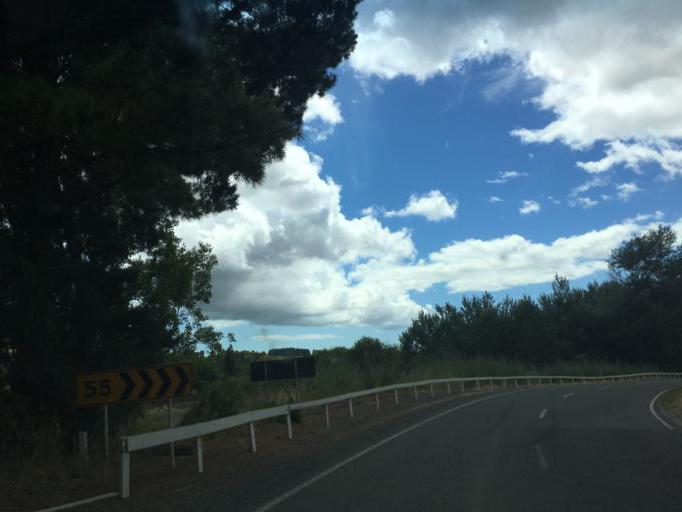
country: NZ
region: Hawke's Bay
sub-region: Hastings District
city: Hastings
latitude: -39.7352
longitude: 176.8993
